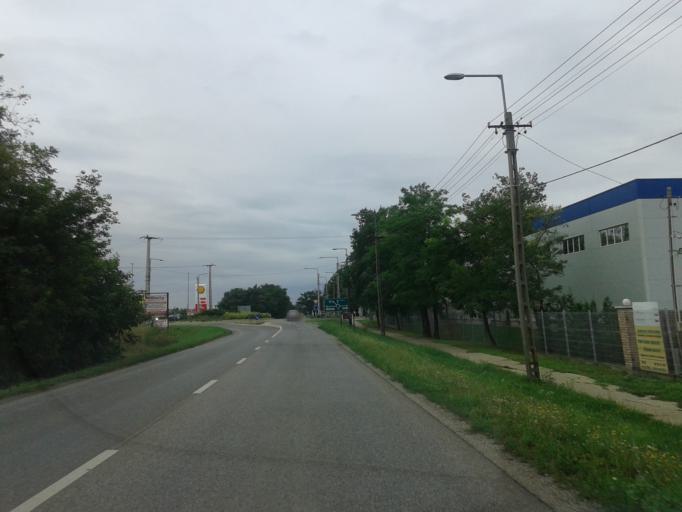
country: HU
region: Pest
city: Halasztelek
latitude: 47.3688
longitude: 18.9961
